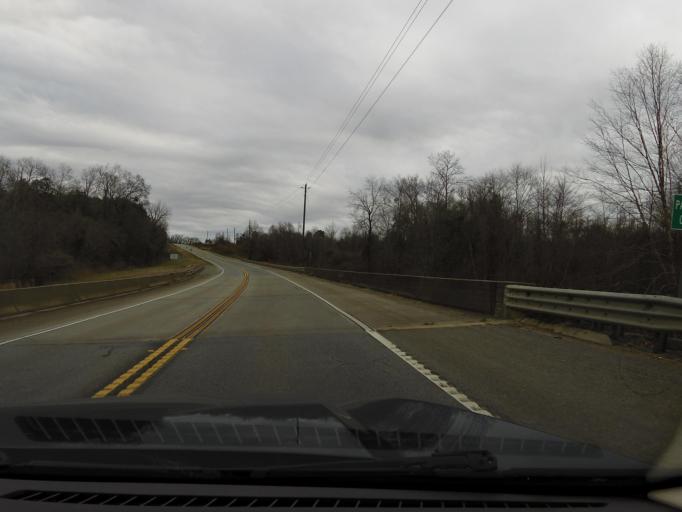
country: US
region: Georgia
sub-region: Randolph County
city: Cuthbert
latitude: 31.7772
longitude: -84.7205
